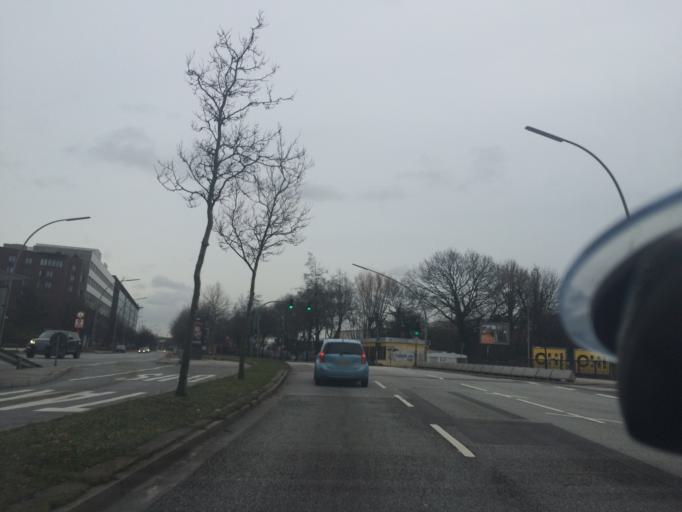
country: DE
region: Hamburg
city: Hamburg-Mitte
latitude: 53.5457
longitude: 10.0158
